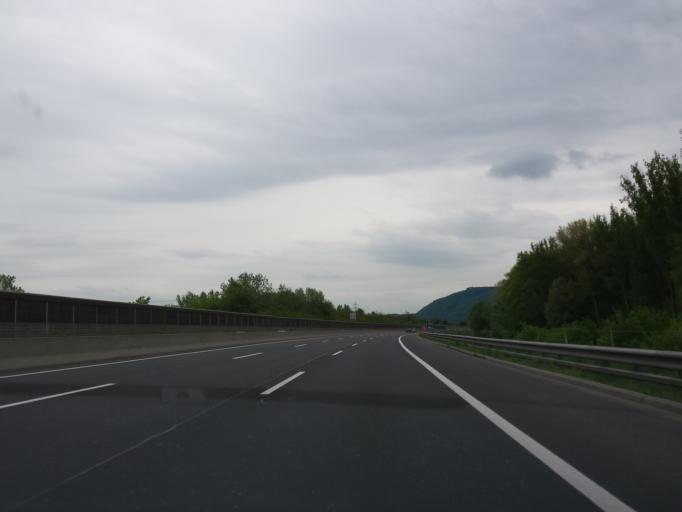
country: AT
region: Lower Austria
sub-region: Politischer Bezirk Korneuburg
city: Bisamberg
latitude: 48.3170
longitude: 16.3450
